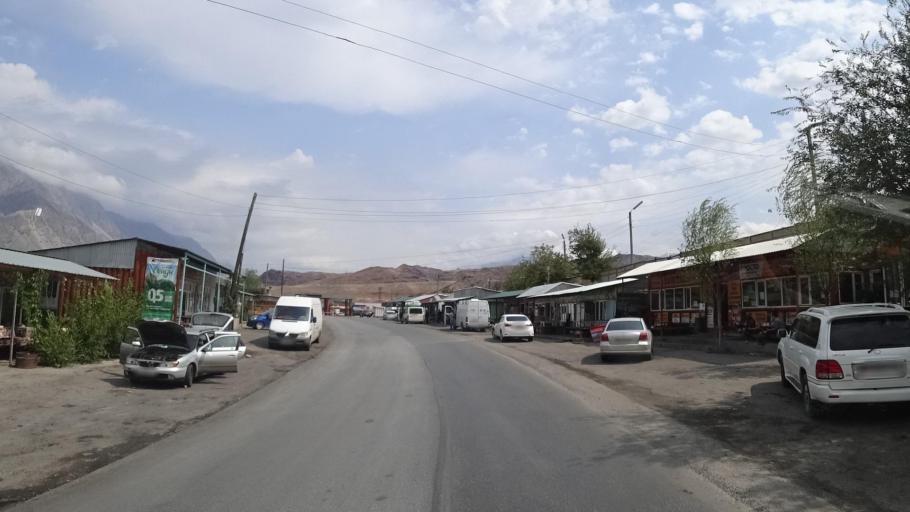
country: KG
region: Jalal-Abad
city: Toktogul
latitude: 41.6126
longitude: 72.6165
